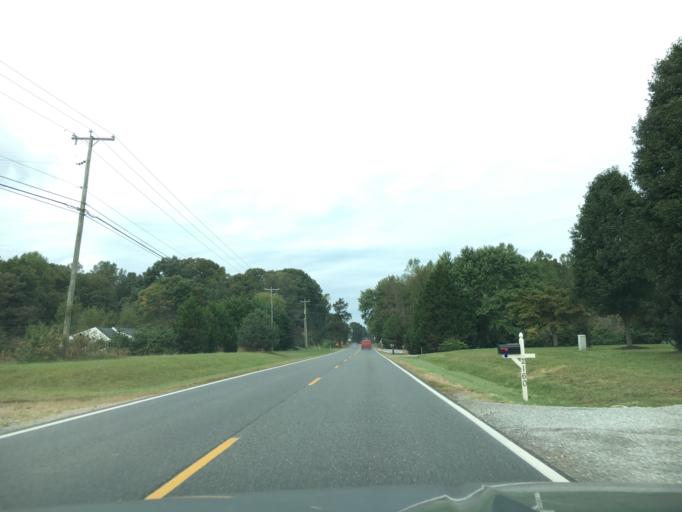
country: US
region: Virginia
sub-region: Goochland County
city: Goochland
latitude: 37.7295
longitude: -77.8350
